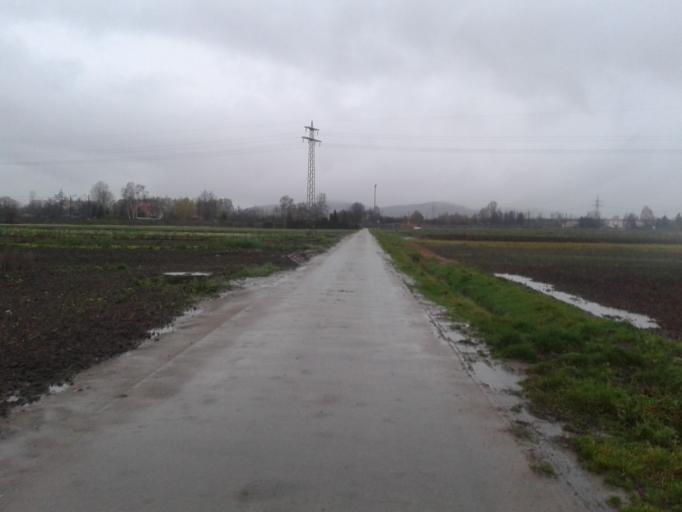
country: DE
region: Bavaria
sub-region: Upper Franconia
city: Bamberg
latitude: 49.9138
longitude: 10.8898
